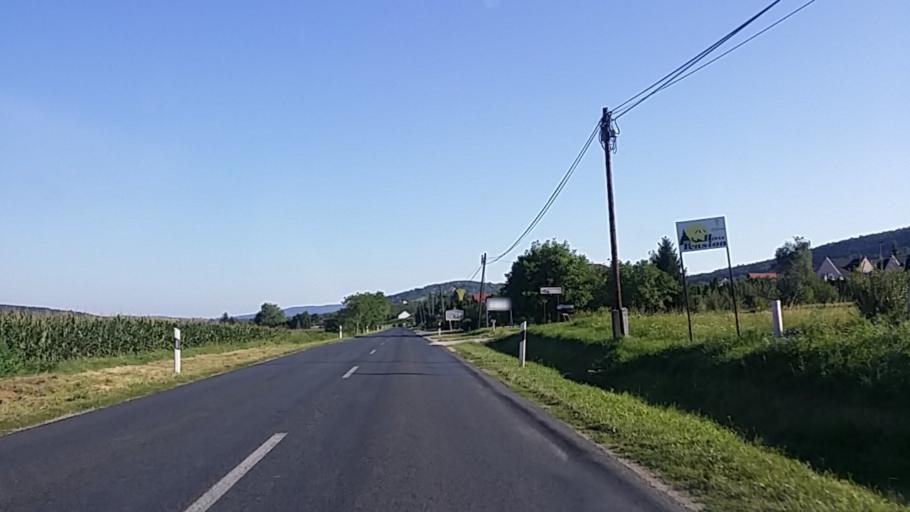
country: HU
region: Zala
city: Cserszegtomaj
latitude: 46.8041
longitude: 17.2066
